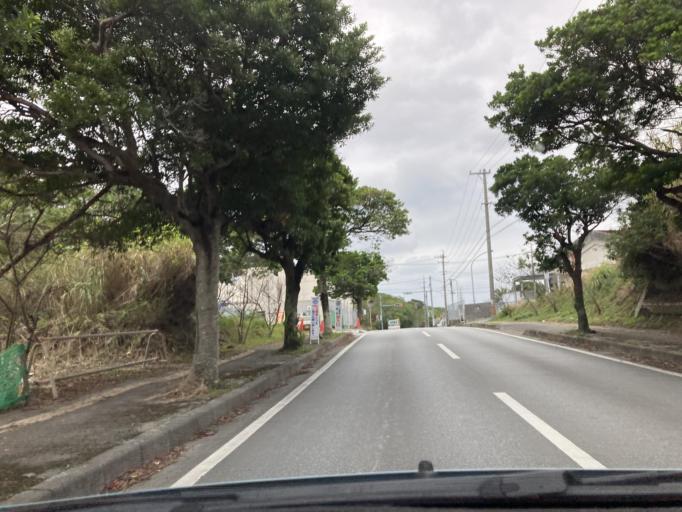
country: JP
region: Okinawa
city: Okinawa
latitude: 26.3457
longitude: 127.8079
